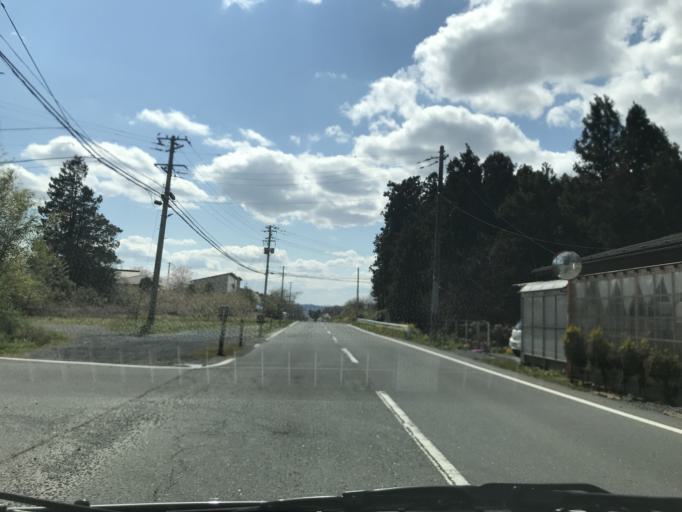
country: JP
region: Miyagi
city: Wakuya
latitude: 38.6334
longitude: 141.2241
